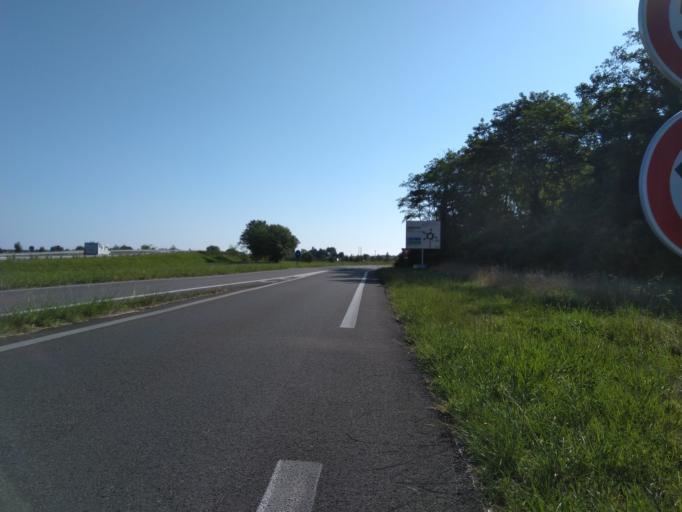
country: FR
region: Aquitaine
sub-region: Departement des Landes
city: Saint-Vincent-de-Paul
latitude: 43.7380
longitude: -1.0199
